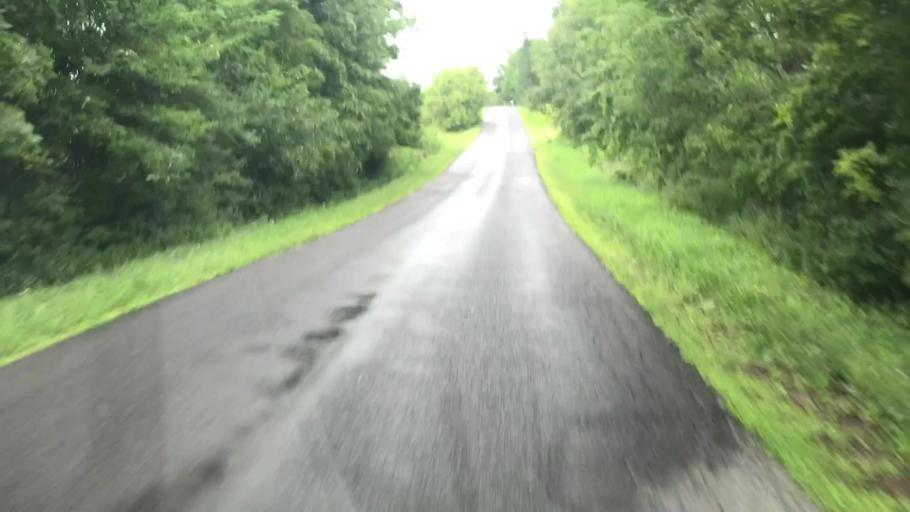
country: US
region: New York
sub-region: Cayuga County
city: Melrose Park
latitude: 42.9626
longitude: -76.5070
